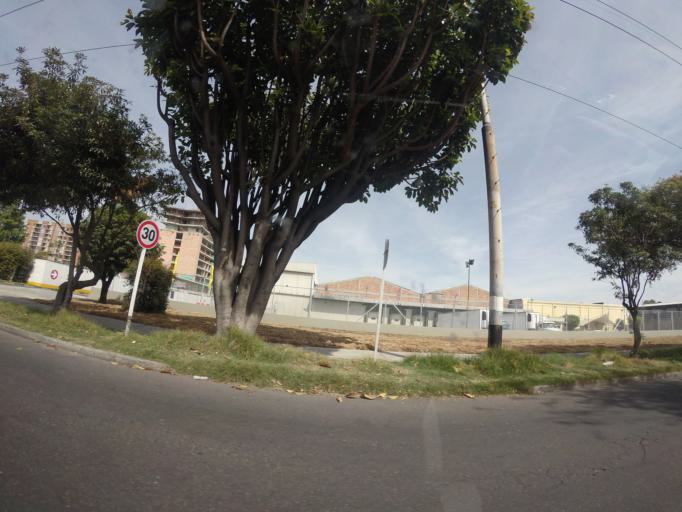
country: CO
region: Bogota D.C.
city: Barrio San Luis
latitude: 4.6928
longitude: -74.0773
